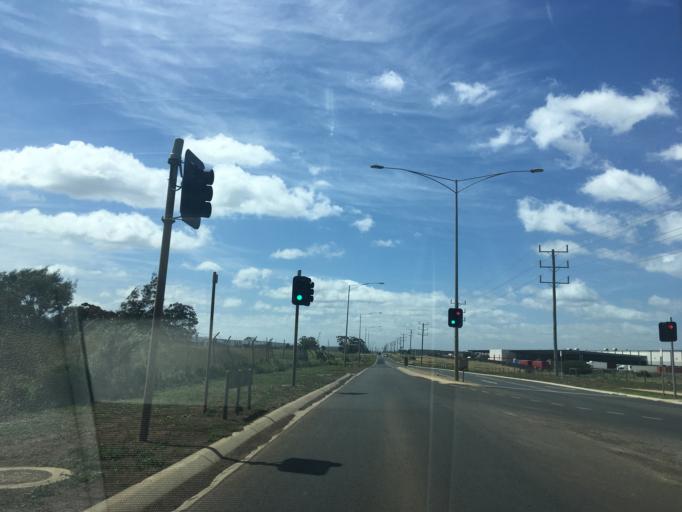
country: AU
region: Victoria
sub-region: Wyndham
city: Truganina
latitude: -37.8234
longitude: 144.7301
